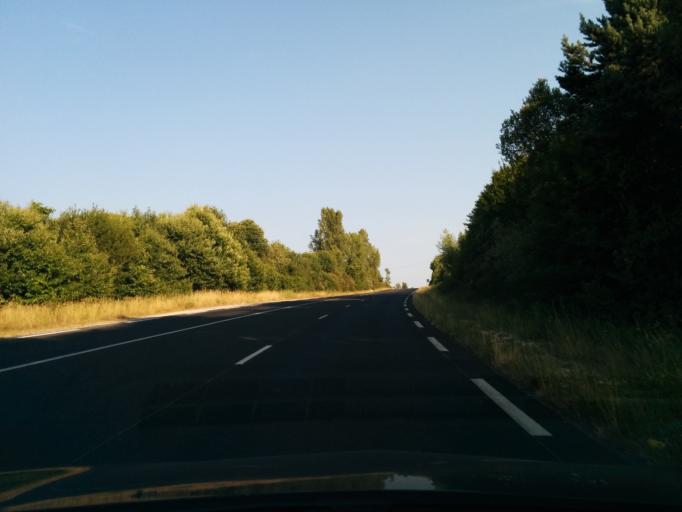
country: FR
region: Midi-Pyrenees
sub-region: Departement du Lot
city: Le Vigan
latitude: 44.7653
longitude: 1.4824
